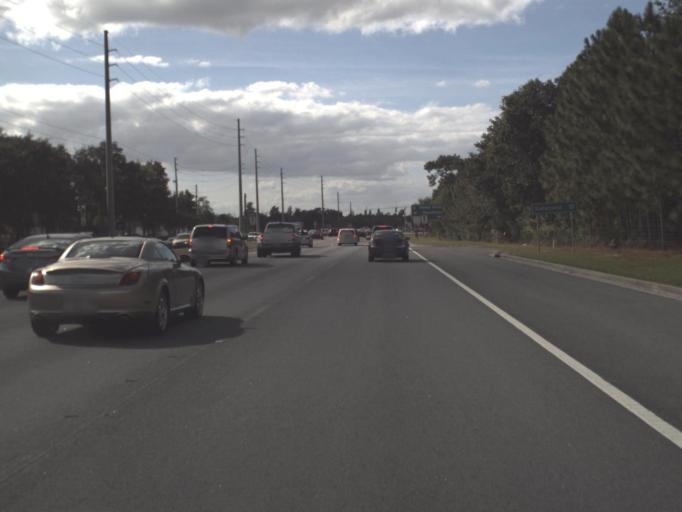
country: US
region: Florida
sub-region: Orange County
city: Hunters Creek
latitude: 28.3374
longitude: -81.4009
